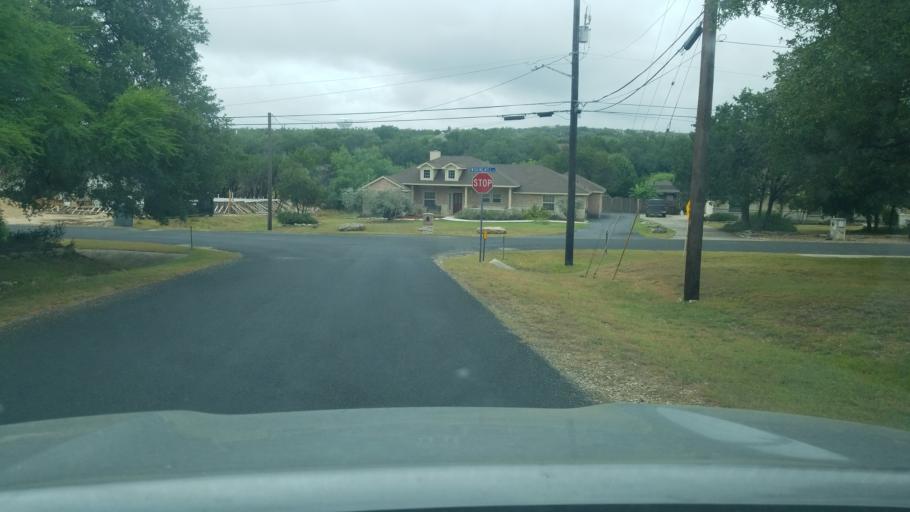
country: US
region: Texas
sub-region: Bexar County
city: Timberwood Park
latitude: 29.6943
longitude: -98.5076
